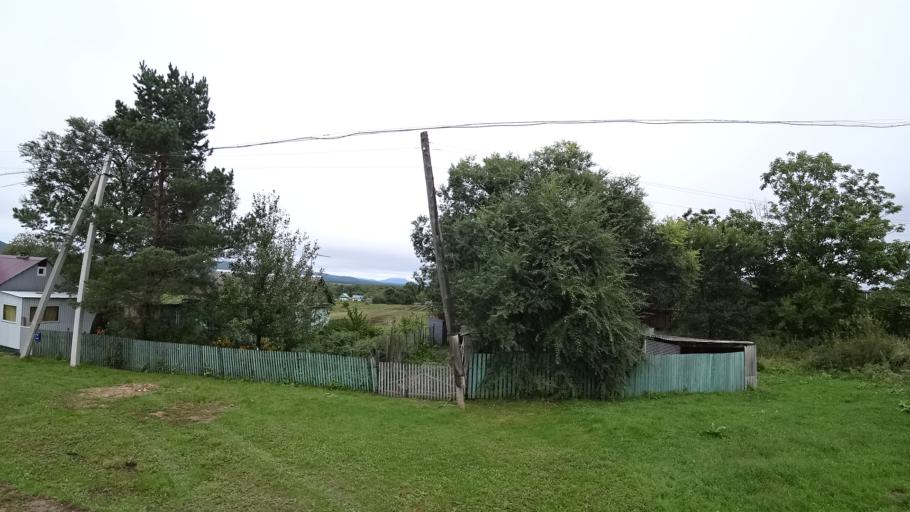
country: RU
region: Primorskiy
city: Monastyrishche
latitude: 44.0850
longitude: 132.5791
